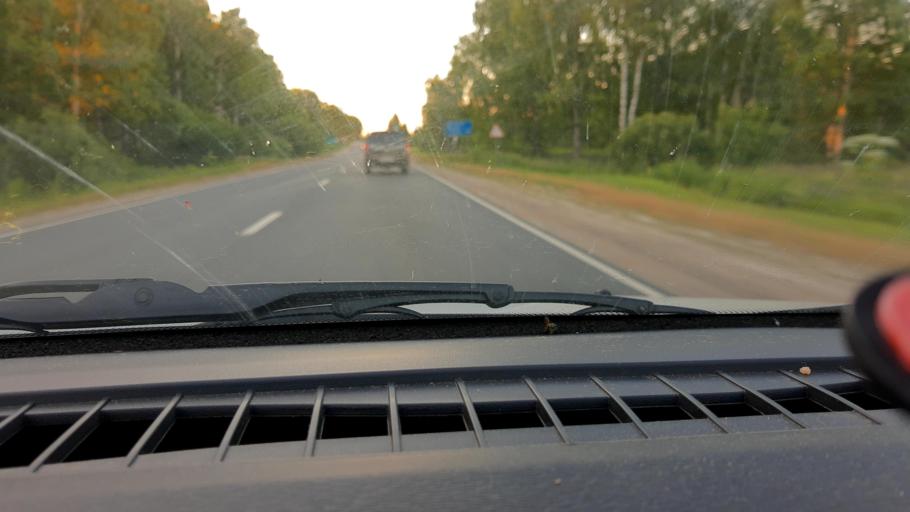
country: RU
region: Nizjnij Novgorod
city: Krasnyye Baki
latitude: 57.0918
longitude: 45.1492
